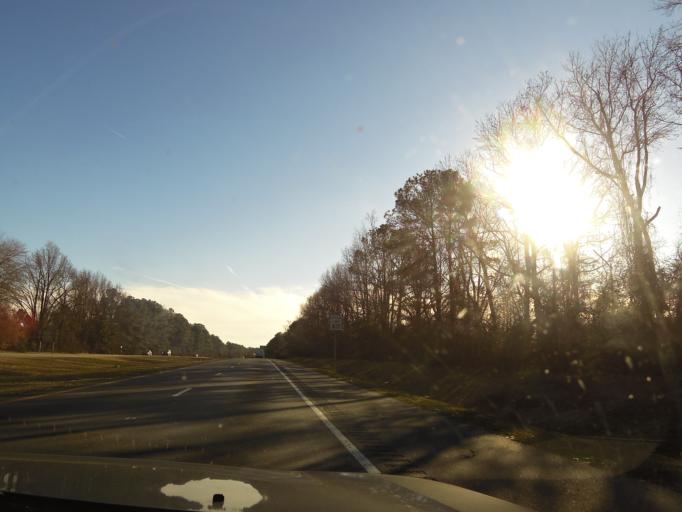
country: US
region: Virginia
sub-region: City of Suffolk
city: Suffolk
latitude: 36.7613
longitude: -76.6086
